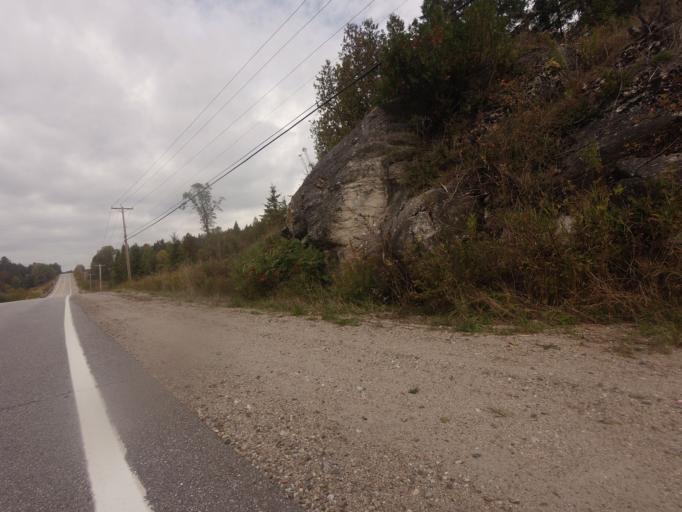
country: CA
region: Quebec
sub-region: Outaouais
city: Wakefield
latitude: 45.9333
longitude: -75.9923
